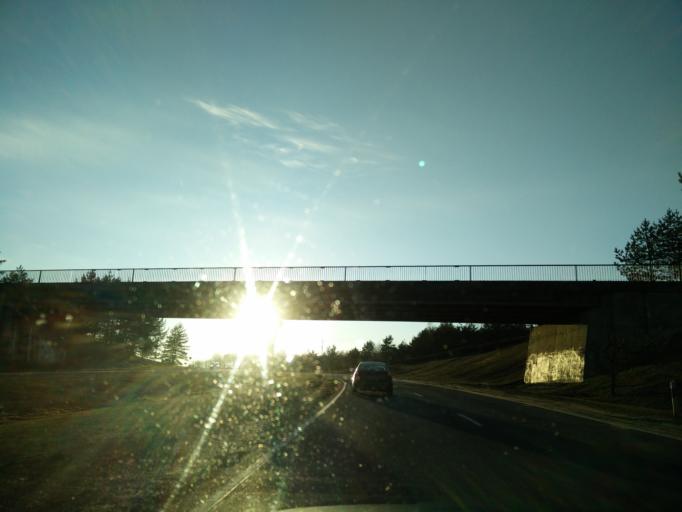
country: LT
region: Vilnius County
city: Rasos
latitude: 54.6937
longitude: 25.3506
